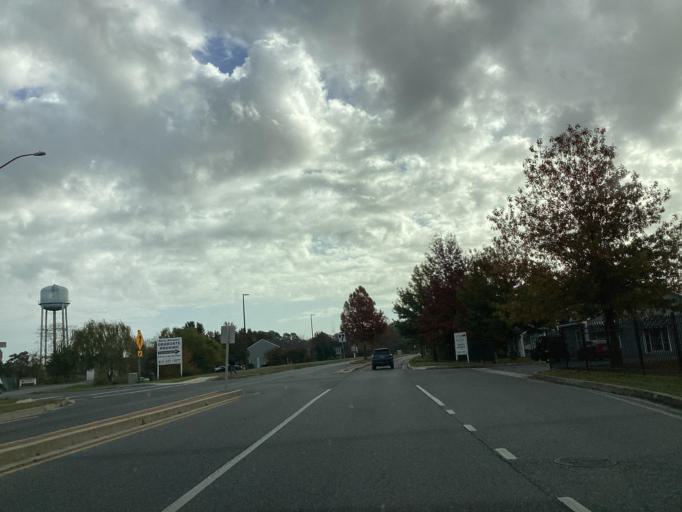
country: US
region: Maryland
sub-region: Somerset County
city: Princess Anne
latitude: 38.2188
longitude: -75.6938
